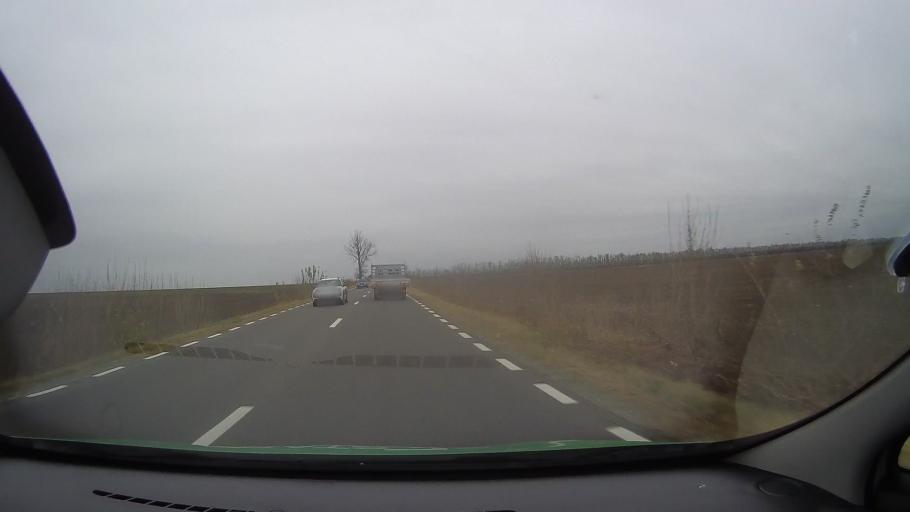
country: RO
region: Ialomita
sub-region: Comuna Gheorghe Lazar
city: Gheorghe Lazar
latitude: 44.6763
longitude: 27.4185
